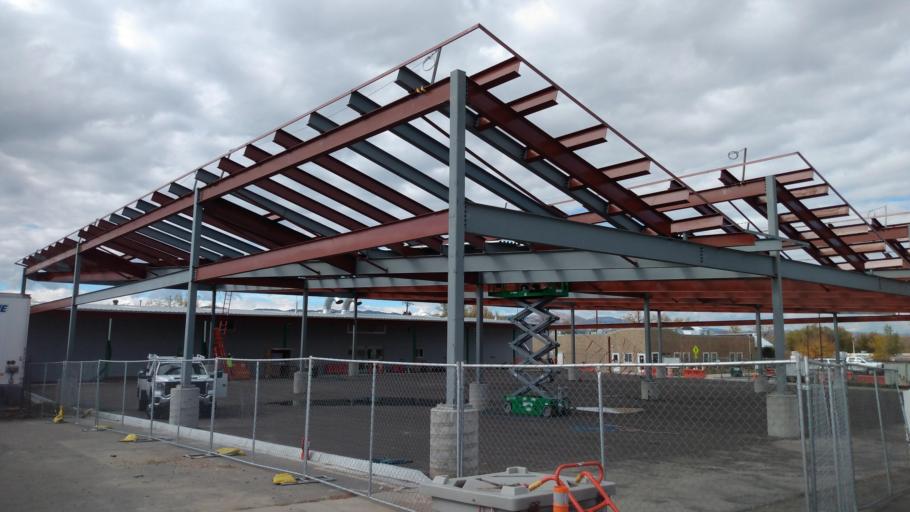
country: US
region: Colorado
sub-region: Boulder County
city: Gunbarrel
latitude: 40.0132
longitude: -105.2039
